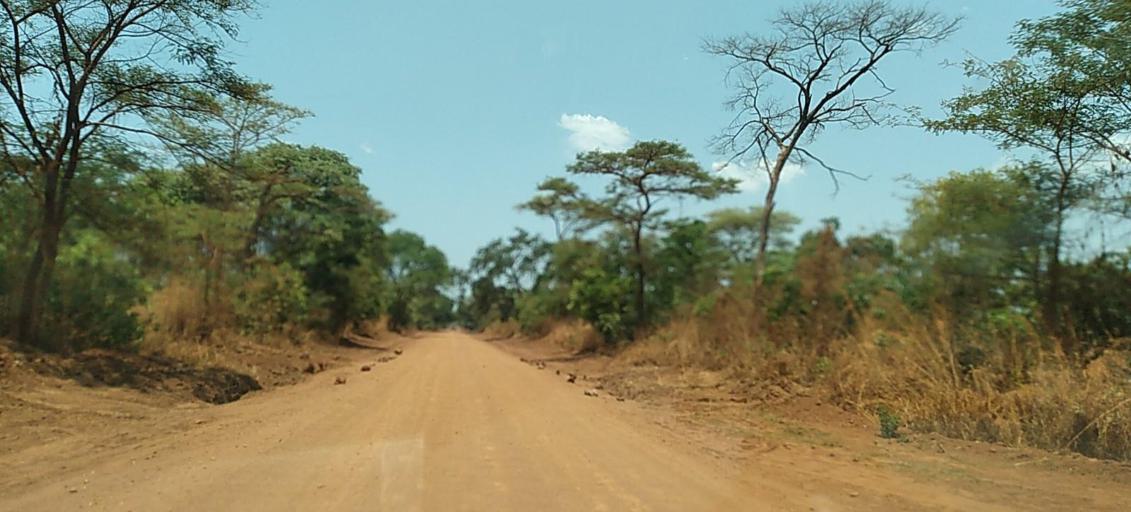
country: ZM
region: Copperbelt
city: Mpongwe
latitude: -13.5154
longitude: 28.0107
